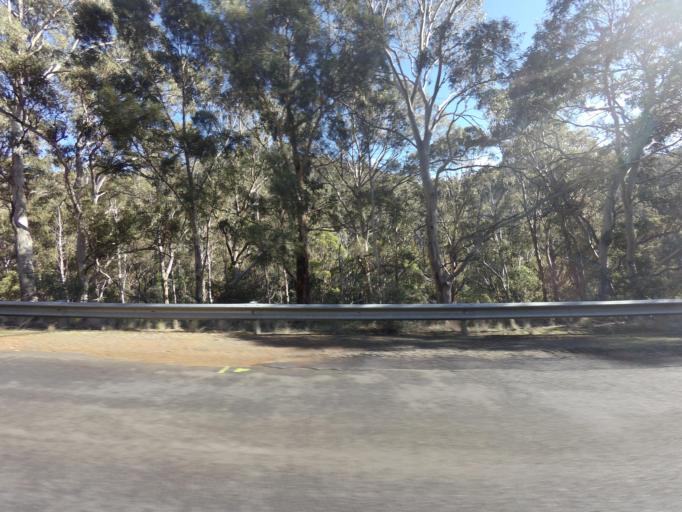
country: AU
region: Tasmania
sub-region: Glenorchy
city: Berriedale
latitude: -42.8242
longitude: 147.2100
